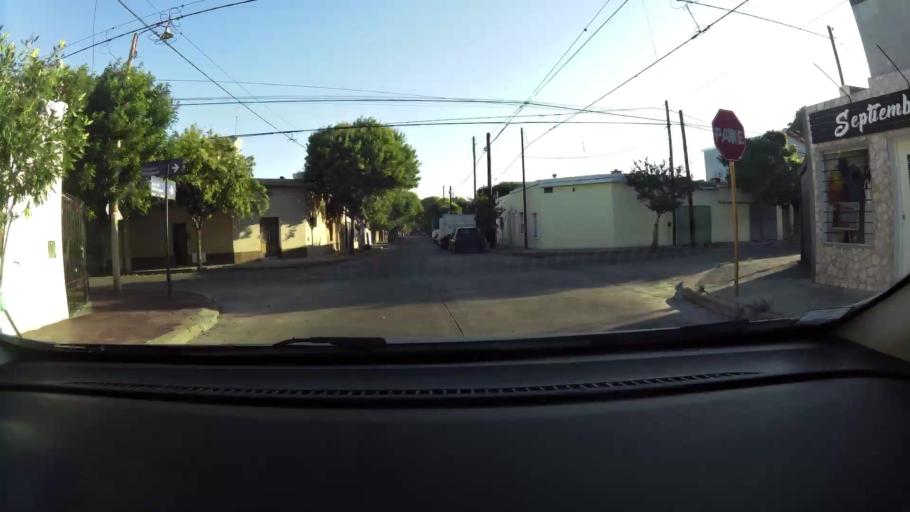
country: AR
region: Cordoba
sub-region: Departamento de Capital
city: Cordoba
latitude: -31.3723
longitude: -64.2103
